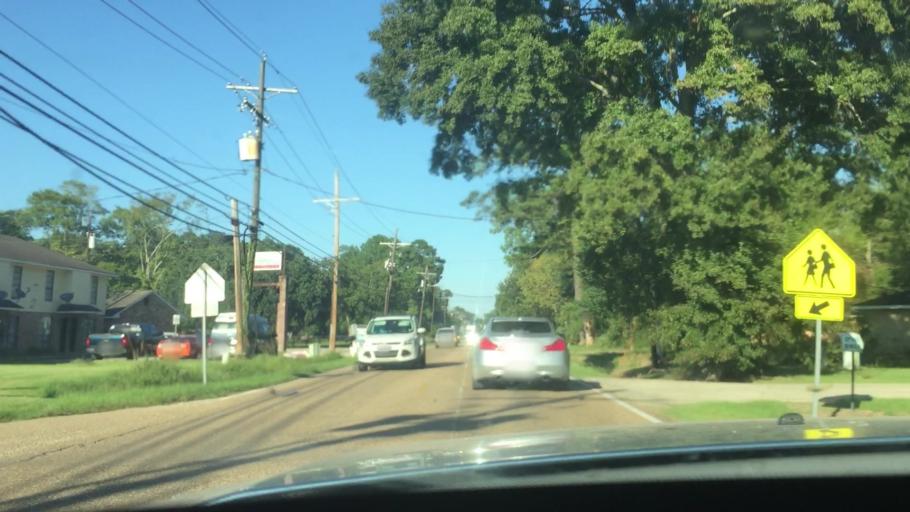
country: US
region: Louisiana
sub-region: East Baton Rouge Parish
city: Monticello
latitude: 30.4572
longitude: -91.0140
